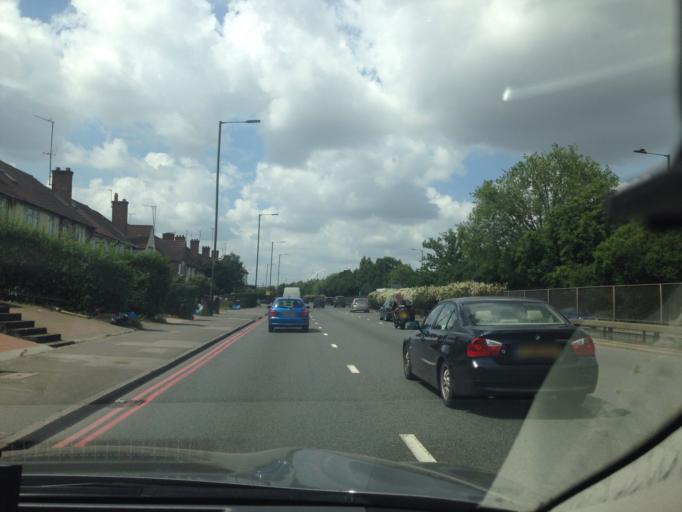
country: GB
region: England
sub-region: Greater London
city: Hendon
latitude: 51.5666
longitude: -0.2463
